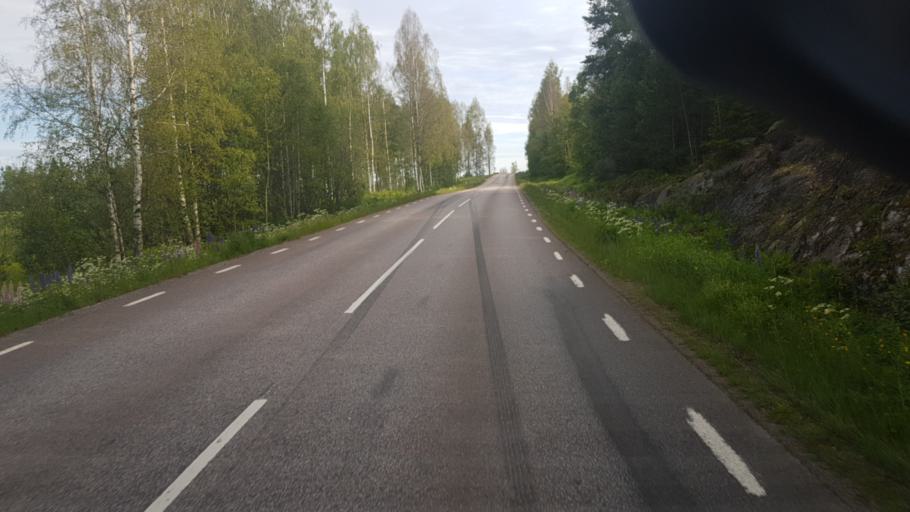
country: SE
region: Vaermland
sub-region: Arvika Kommun
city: Arvika
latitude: 59.7652
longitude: 12.6129
